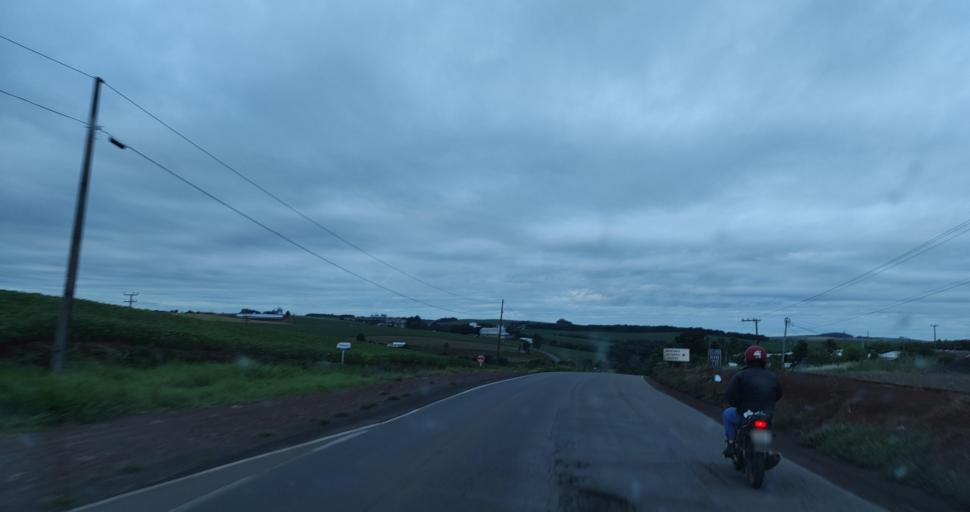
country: BR
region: Santa Catarina
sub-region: Xanxere
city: Xanxere
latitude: -26.7442
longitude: -52.3968
